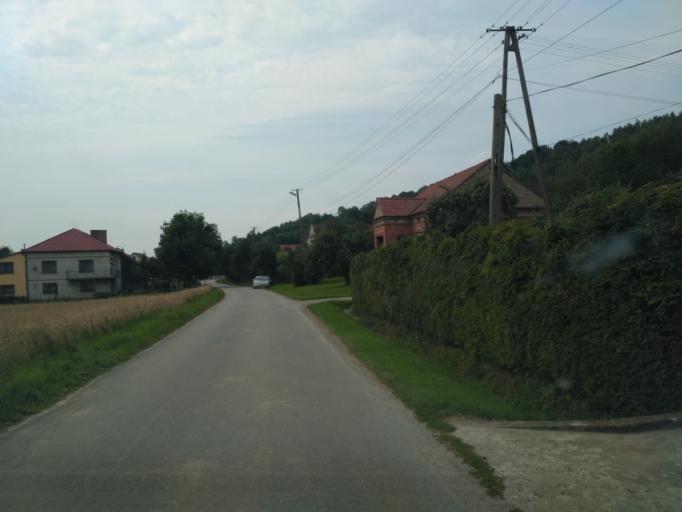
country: PL
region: Subcarpathian Voivodeship
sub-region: Powiat strzyzowski
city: Strzyzow
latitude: 49.8483
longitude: 21.8166
